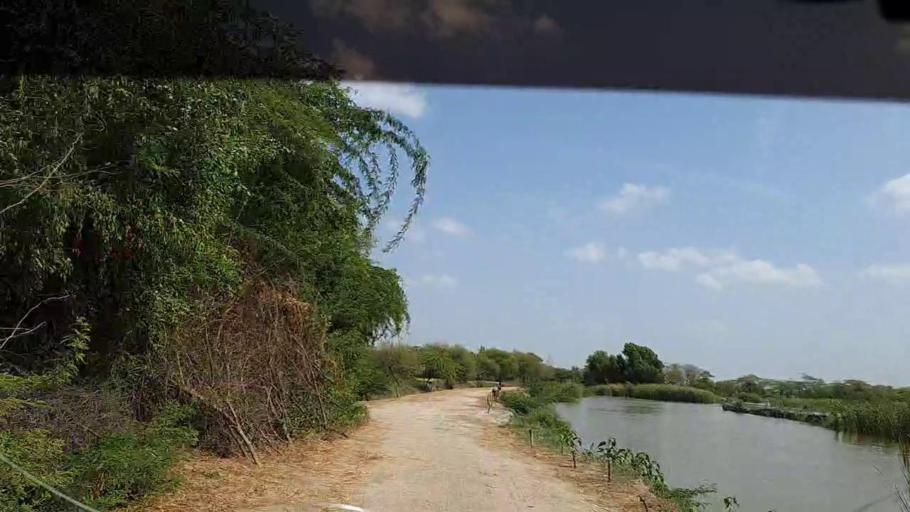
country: PK
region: Sindh
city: Badin
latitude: 24.5894
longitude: 68.8036
